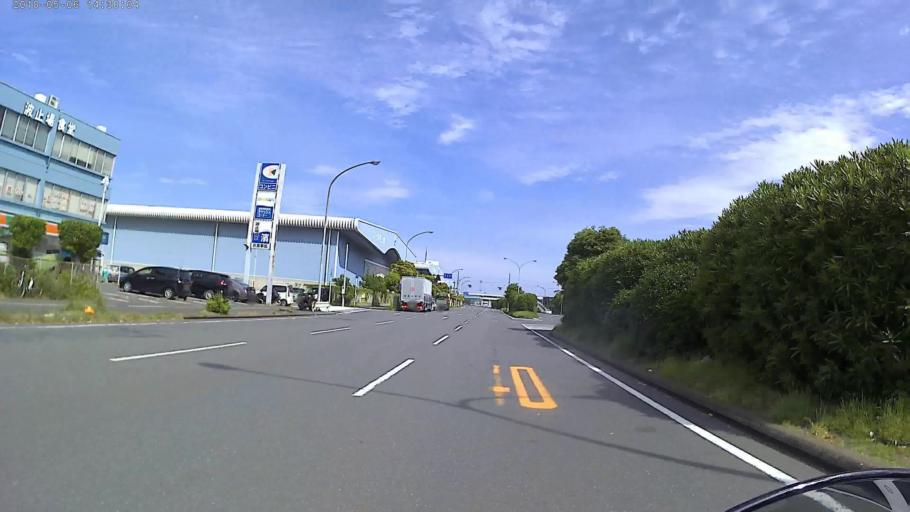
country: JP
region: Kanagawa
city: Yokohama
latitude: 35.4293
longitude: 139.6753
